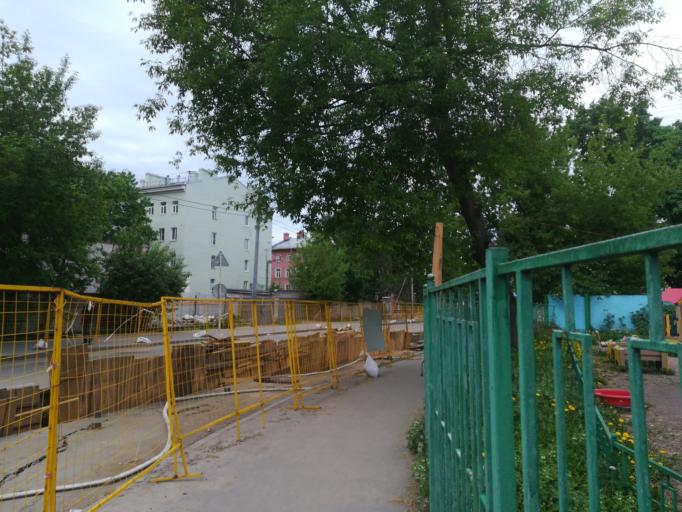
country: RU
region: St.-Petersburg
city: Vasyl'evsky Ostrov
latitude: 59.9518
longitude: 30.2558
